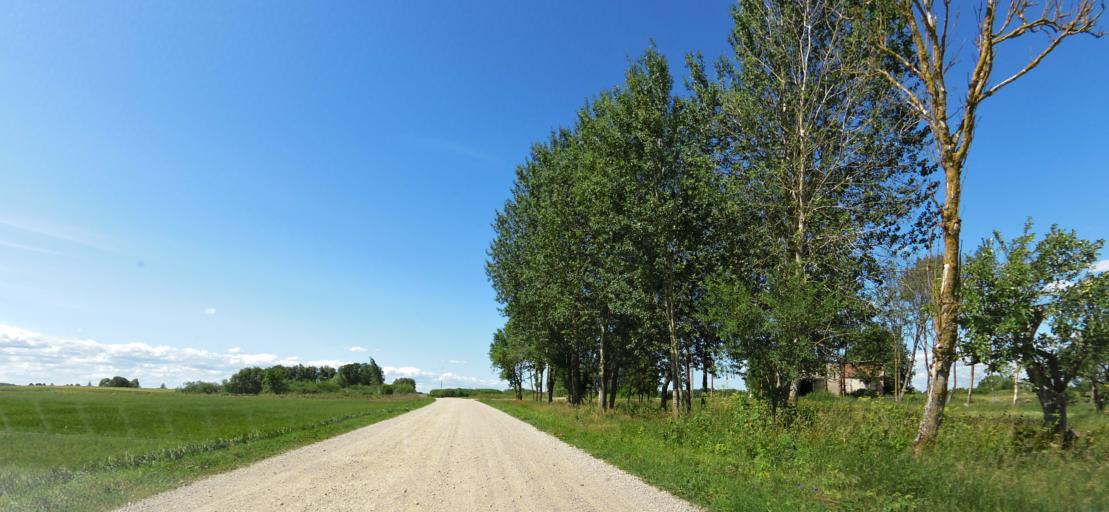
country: LV
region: Bauskas Rajons
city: Bauska
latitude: 56.2854
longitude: 24.3402
